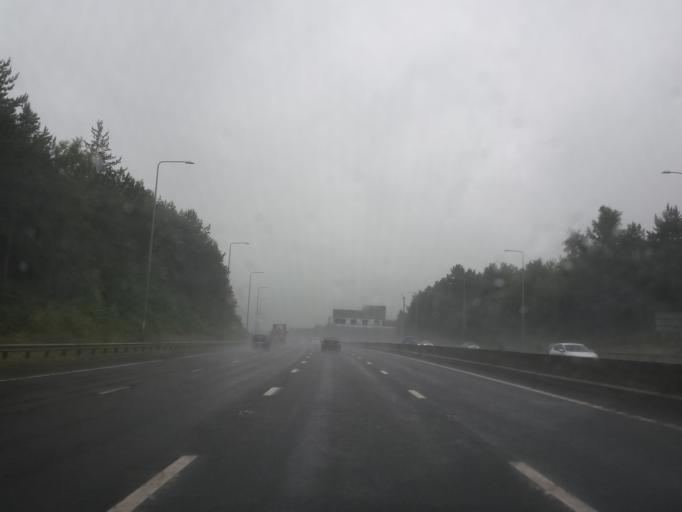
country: GB
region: England
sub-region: Nottinghamshire
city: Kirkby in Ashfield
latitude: 53.0444
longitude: -1.2560
